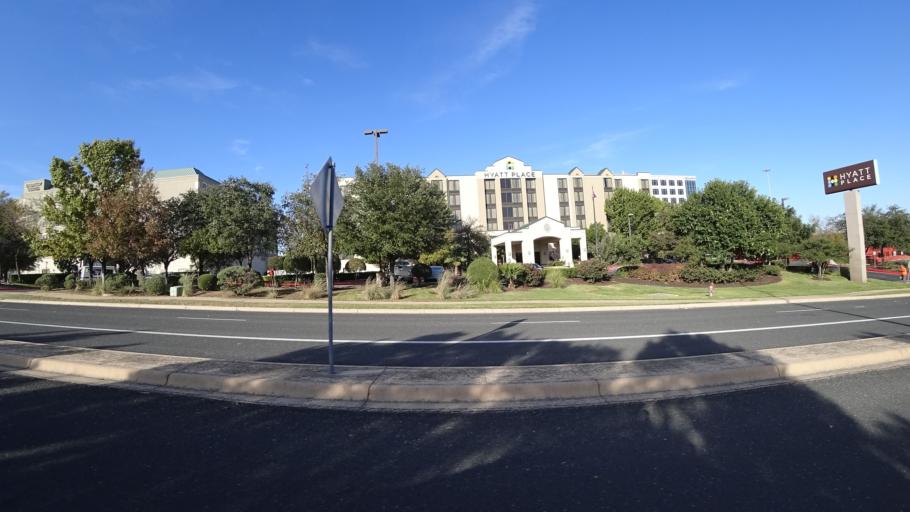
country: US
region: Texas
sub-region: Williamson County
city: Jollyville
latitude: 30.3843
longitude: -97.7380
